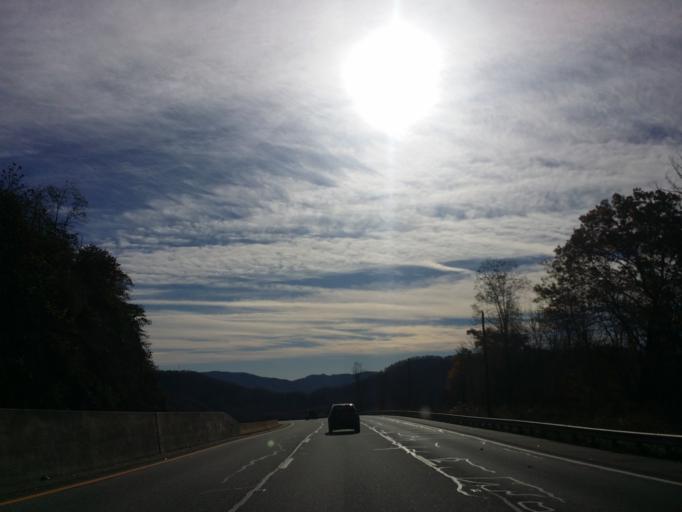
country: US
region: North Carolina
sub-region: Buncombe County
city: Black Mountain
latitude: 35.6235
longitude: -82.2347
